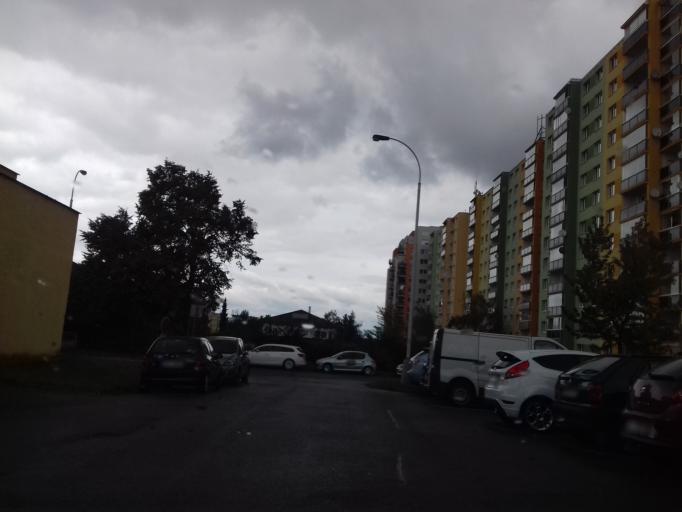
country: CZ
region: Praha
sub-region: Praha 4
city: Hodkovicky
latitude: 50.0180
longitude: 14.4454
